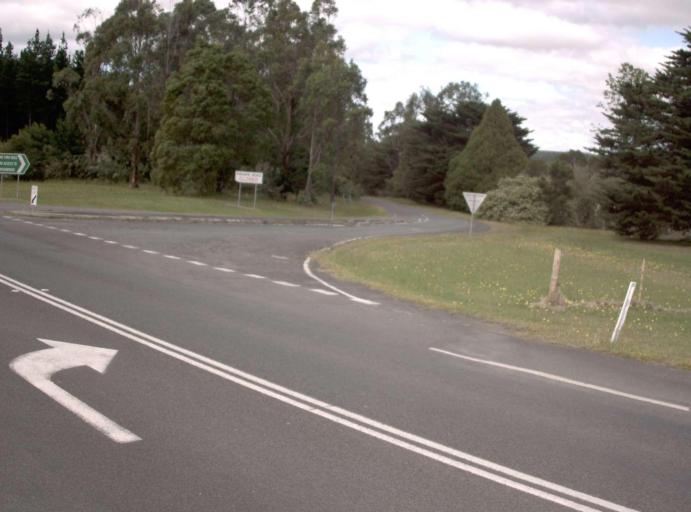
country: AU
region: Victoria
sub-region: Latrobe
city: Morwell
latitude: -38.1913
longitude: 146.4507
